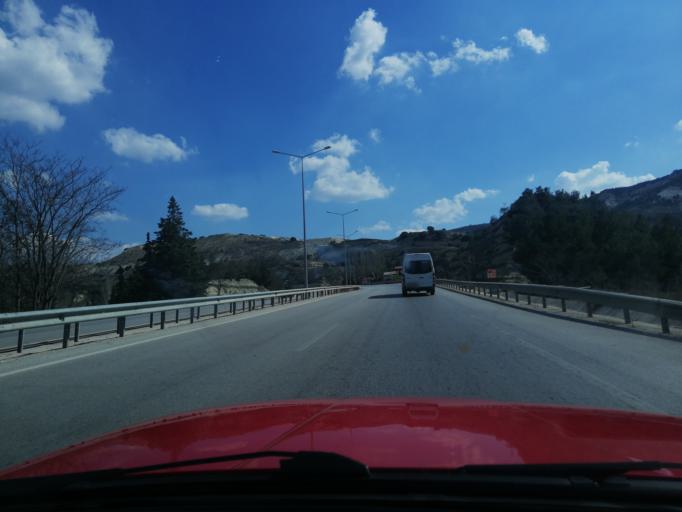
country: TR
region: Burdur
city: Burdur
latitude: 37.7040
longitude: 30.3066
